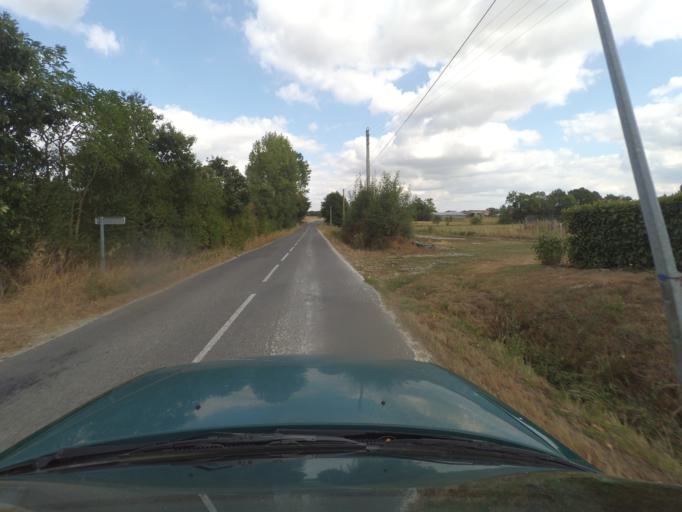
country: FR
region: Pays de la Loire
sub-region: Departement de la Loire-Atlantique
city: La Planche
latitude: 47.0043
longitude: -1.4095
